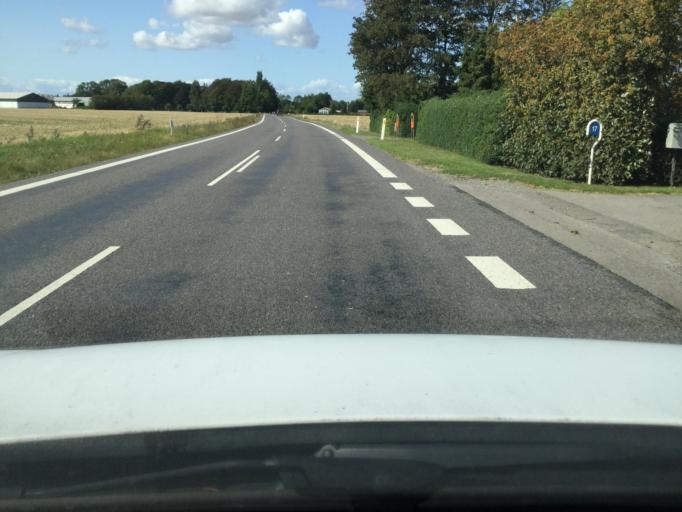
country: DK
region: Zealand
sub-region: Lolland Kommune
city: Rodby
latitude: 54.7950
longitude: 11.2766
